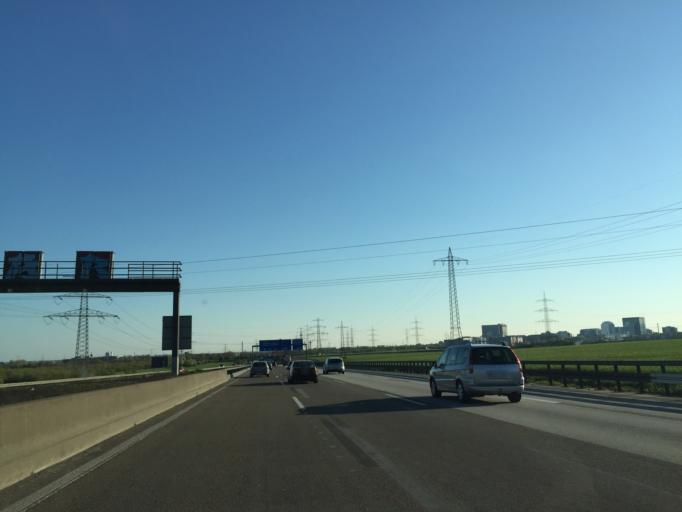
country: DE
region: Hesse
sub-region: Regierungsbezirk Darmstadt
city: Eschborn
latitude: 50.1506
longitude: 8.5995
